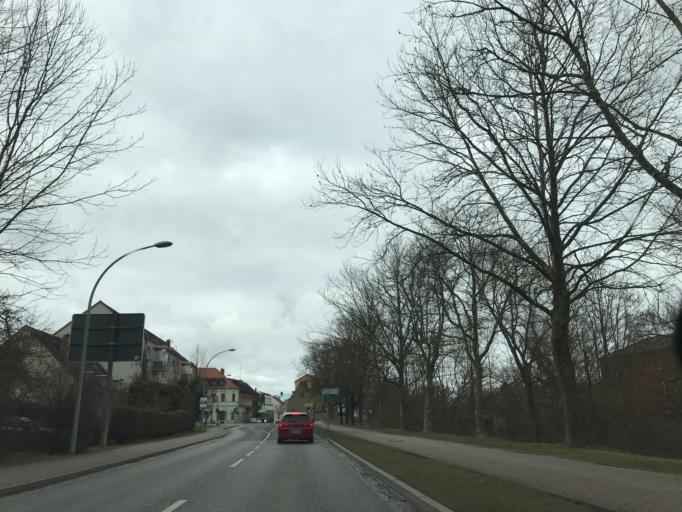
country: DE
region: Brandenburg
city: Luebben
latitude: 51.9405
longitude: 13.8938
